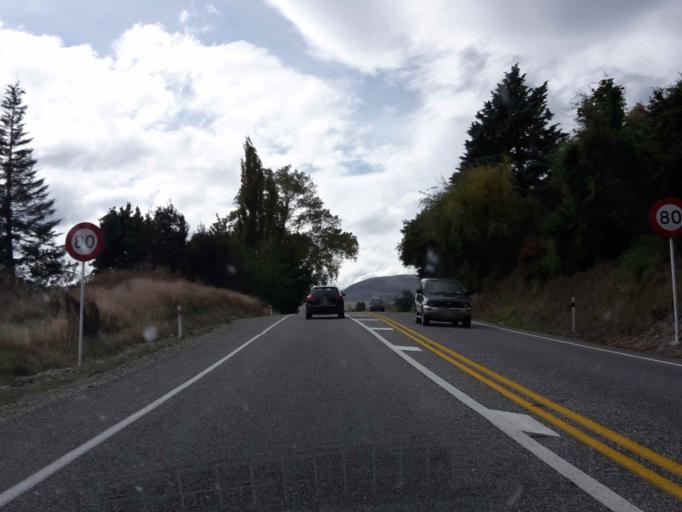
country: NZ
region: Otago
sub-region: Queenstown-Lakes District
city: Arrowtown
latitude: -44.9946
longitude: 168.8050
